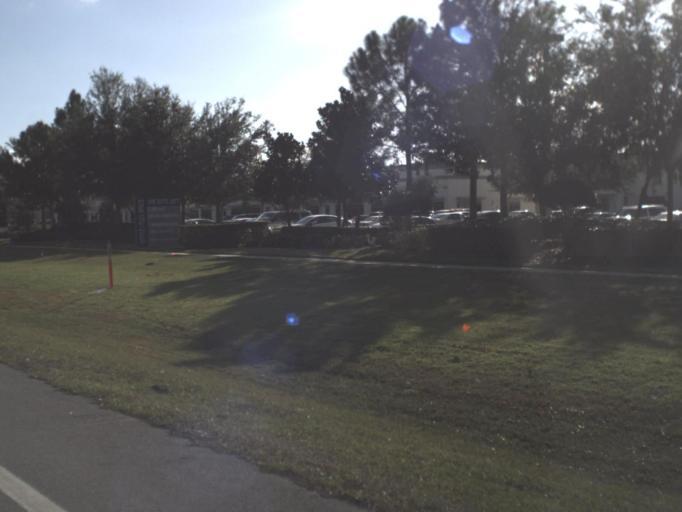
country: US
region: Florida
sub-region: Volusia County
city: Holly Hill
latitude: 29.2132
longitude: -81.0905
